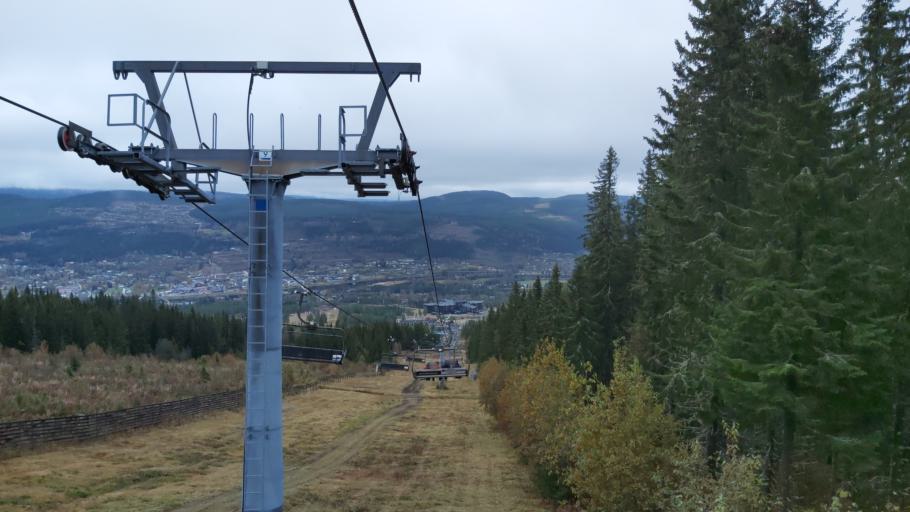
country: NO
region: Hedmark
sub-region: Trysil
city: Innbygda
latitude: 61.3083
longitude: 12.2194
